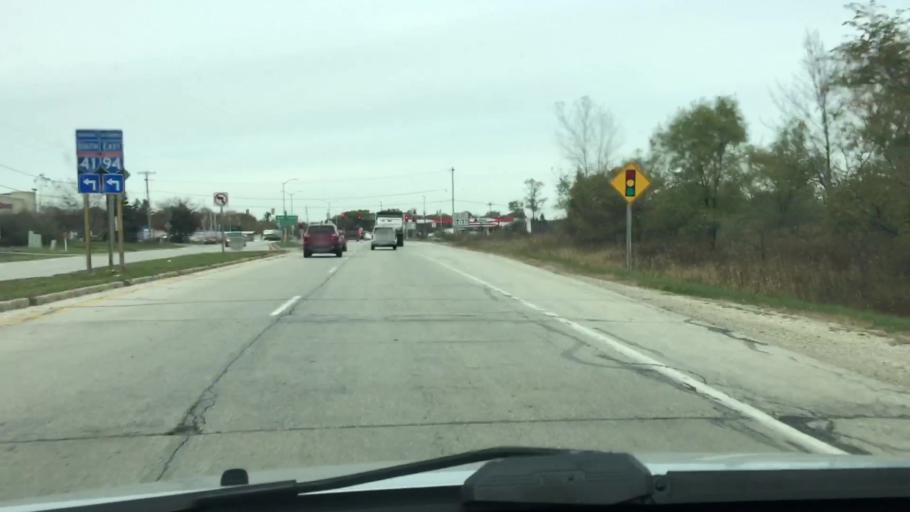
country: US
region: Wisconsin
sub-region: Milwaukee County
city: Franklin
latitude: 42.8876
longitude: -88.0365
